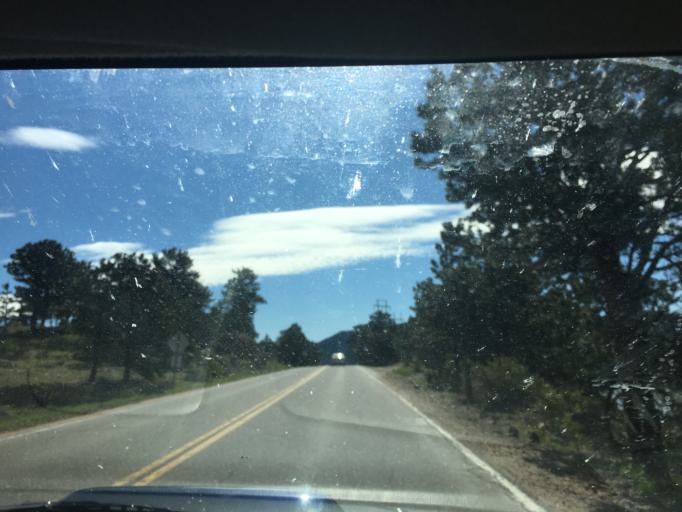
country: US
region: Colorado
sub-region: Larimer County
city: Estes Park
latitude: 40.3470
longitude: -105.5350
